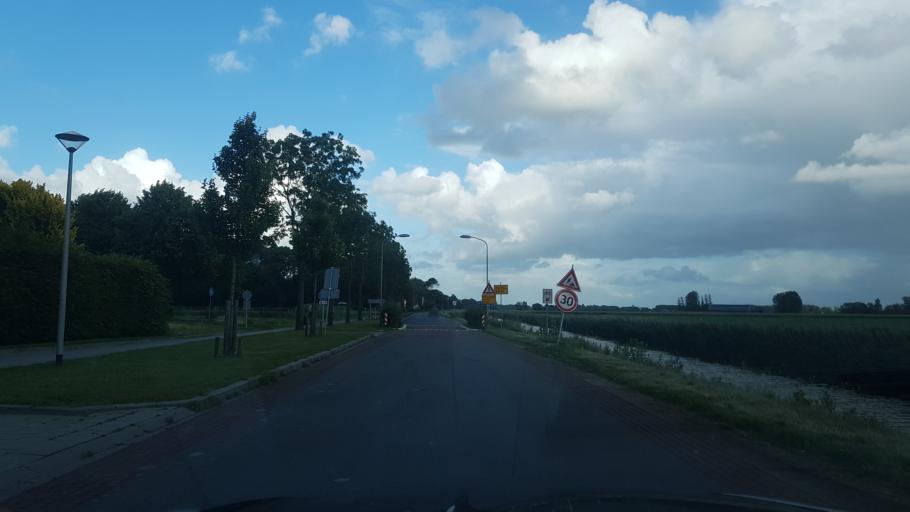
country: NL
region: Groningen
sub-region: Gemeente Appingedam
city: Appingedam
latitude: 53.3271
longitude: 6.7497
